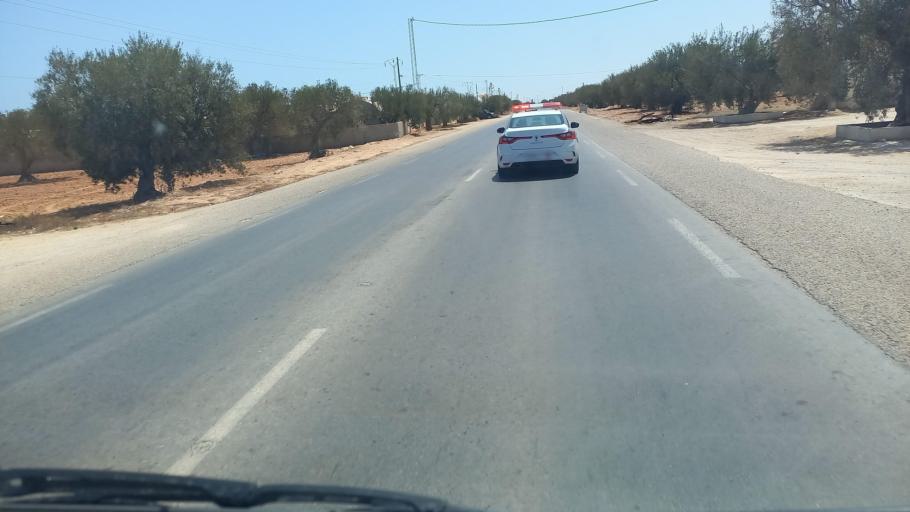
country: TN
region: Madanin
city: Zarzis
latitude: 33.5464
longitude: 11.0715
